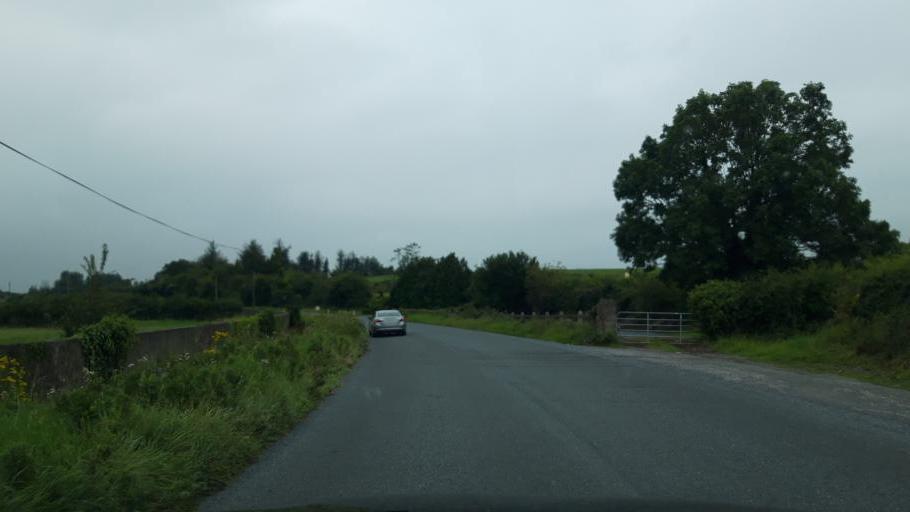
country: IE
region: Munster
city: Fethard
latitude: 52.4569
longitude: -7.7065
